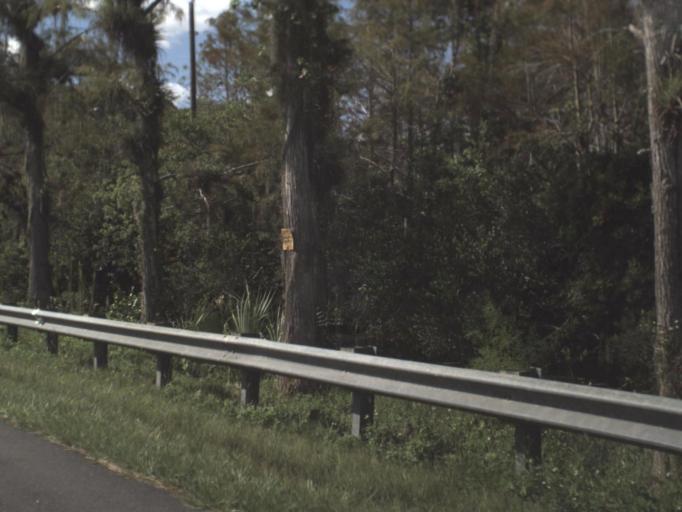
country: US
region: Florida
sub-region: Miami-Dade County
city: Kendall West
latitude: 25.8460
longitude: -80.9246
